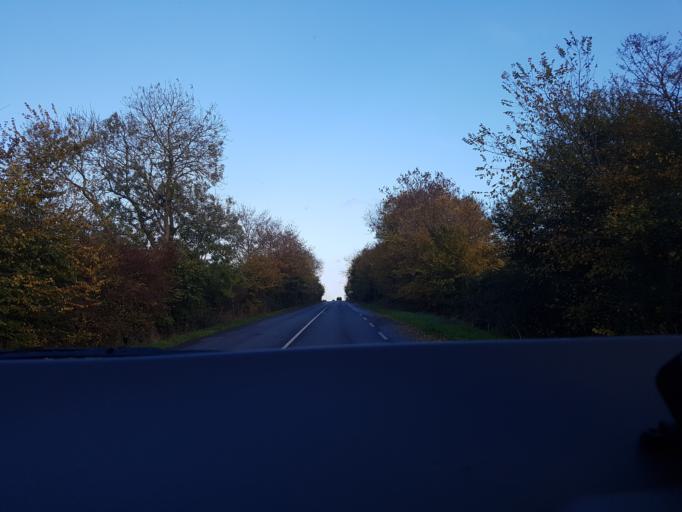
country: FR
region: Lower Normandy
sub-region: Departement du Calvados
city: Troarn
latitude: 49.1793
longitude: -0.1970
